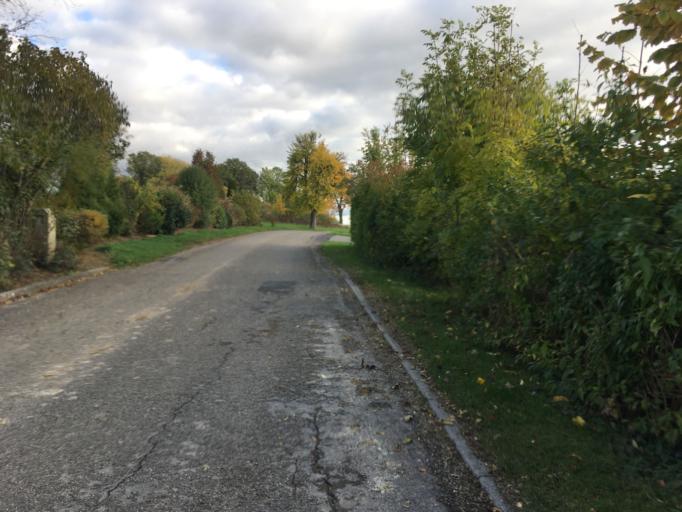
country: DE
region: Baden-Wuerttemberg
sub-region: Regierungsbezirk Stuttgart
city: Kupferzell
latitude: 49.2380
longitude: 9.6660
